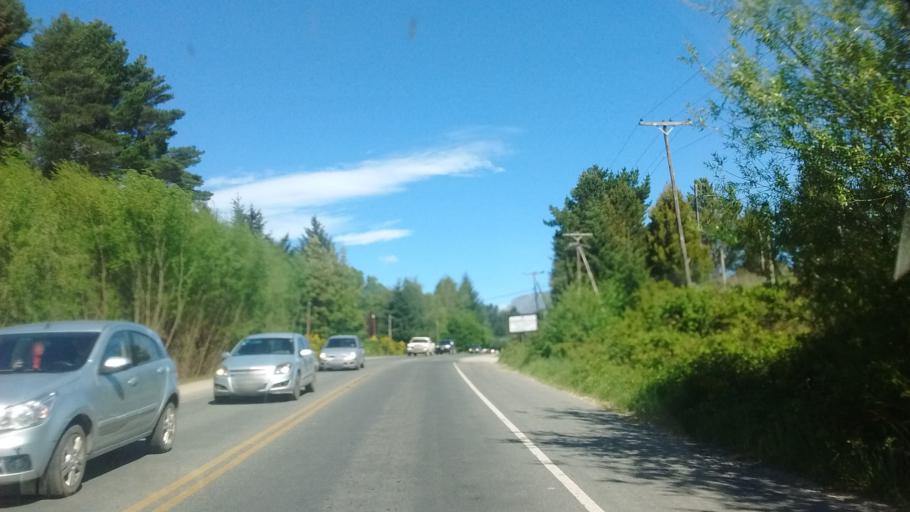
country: AR
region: Chubut
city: Lago Puelo
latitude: -42.0313
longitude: -71.5678
